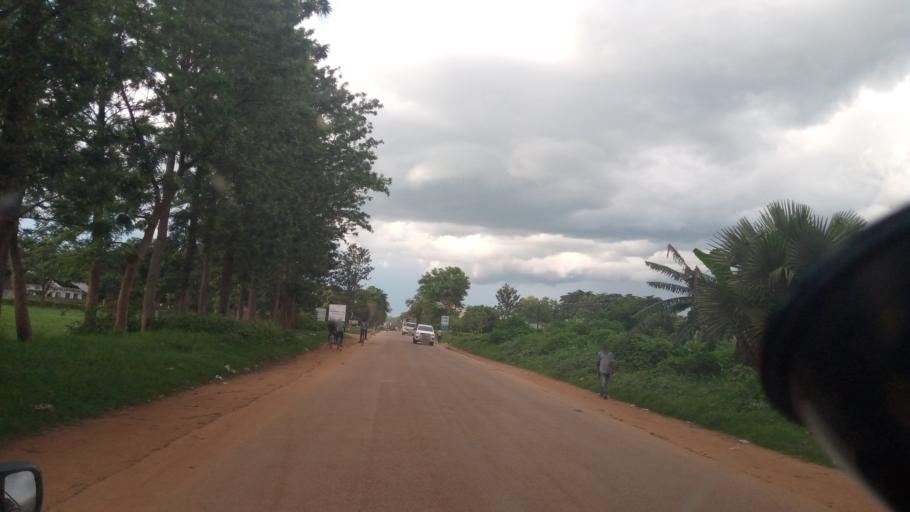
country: UG
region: Northern Region
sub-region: Lira District
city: Lira
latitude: 2.2578
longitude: 32.9070
